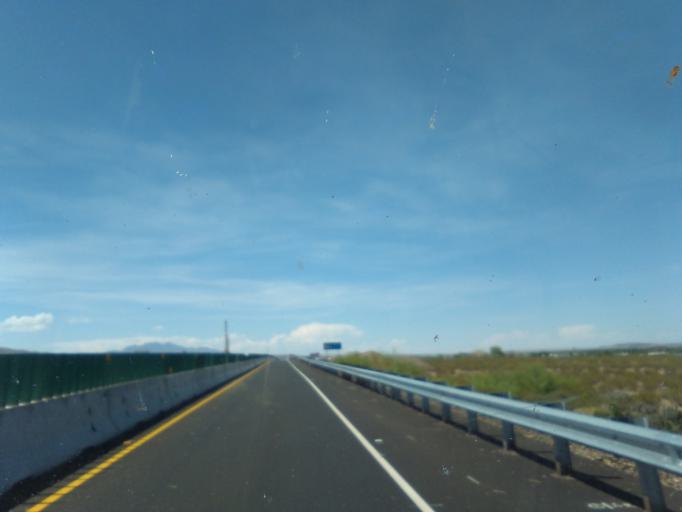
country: US
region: New Mexico
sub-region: Socorro County
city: Socorro
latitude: 34.1450
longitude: -106.9135
